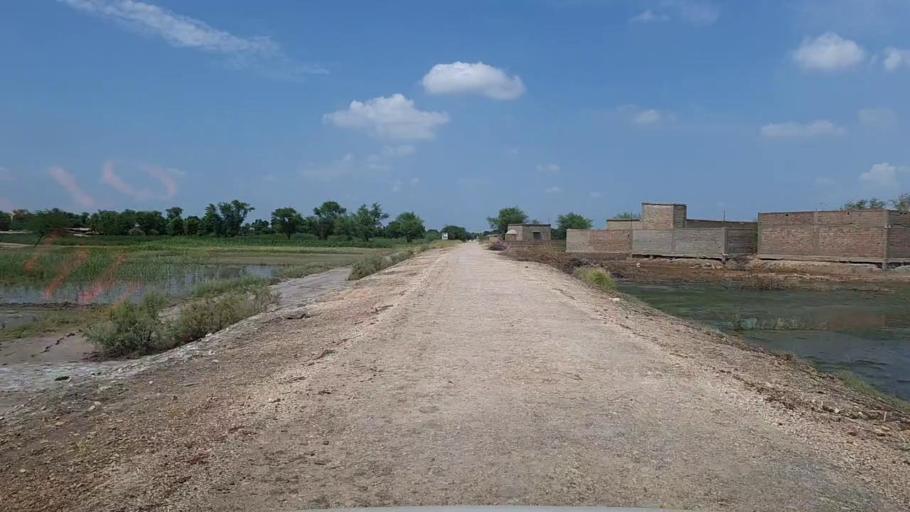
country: PK
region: Sindh
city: Bhiria
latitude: 26.9739
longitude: 68.2404
